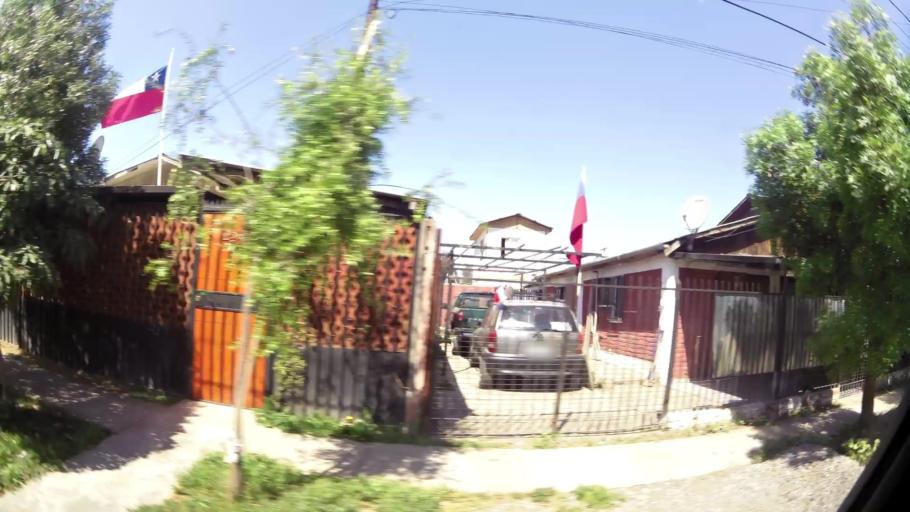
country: CL
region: Santiago Metropolitan
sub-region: Provincia de Talagante
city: Penaflor
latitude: -33.5735
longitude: -70.8101
